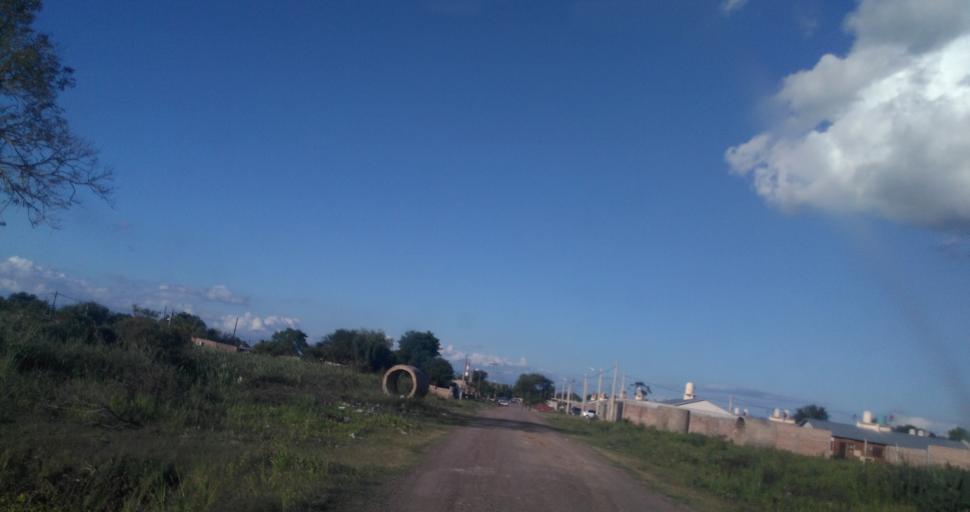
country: AR
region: Chaco
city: Fontana
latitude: -27.4260
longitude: -59.0407
